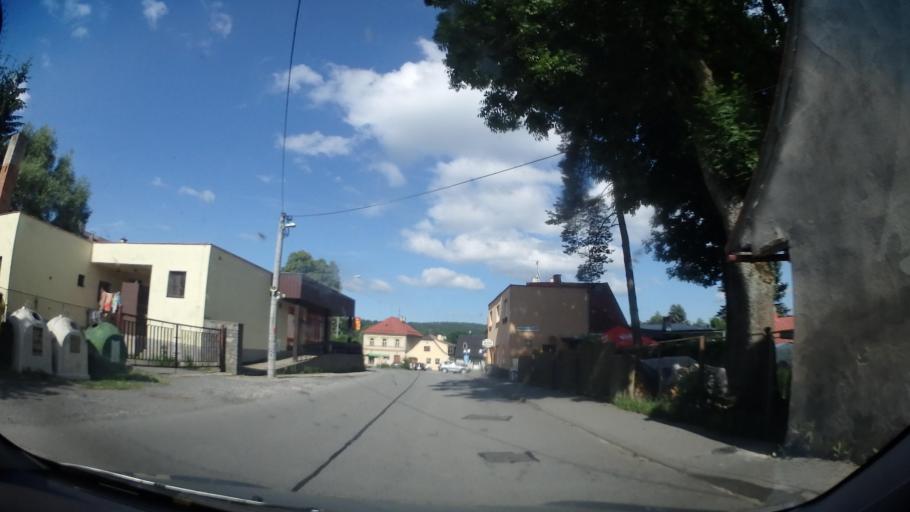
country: CZ
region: Vysocina
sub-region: Okres Zd'ar nad Sazavou
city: Svratka
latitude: 49.7106
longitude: 16.0306
